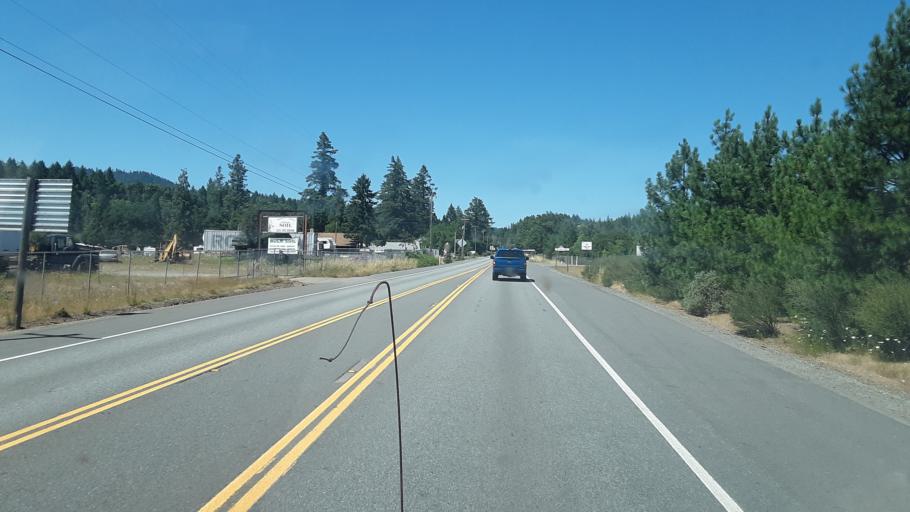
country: US
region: Oregon
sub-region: Josephine County
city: Cave Junction
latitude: 42.2808
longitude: -123.6154
